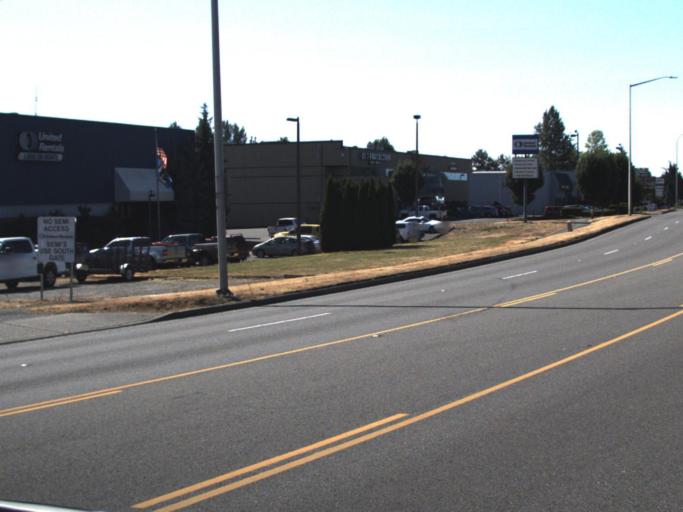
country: US
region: Washington
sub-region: King County
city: Tukwila
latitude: 47.4447
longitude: -122.2460
